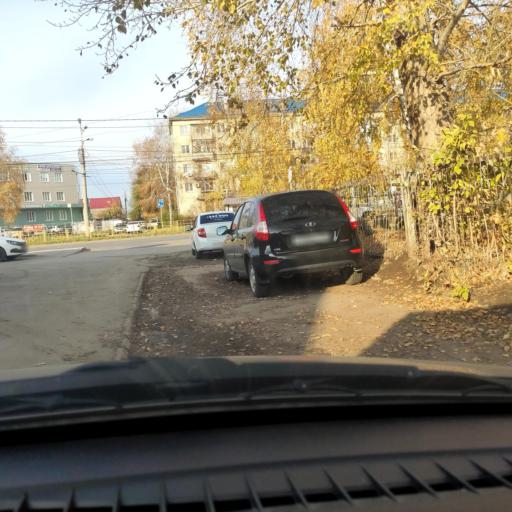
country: RU
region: Samara
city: Tol'yatti
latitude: 53.5300
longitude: 49.4109
